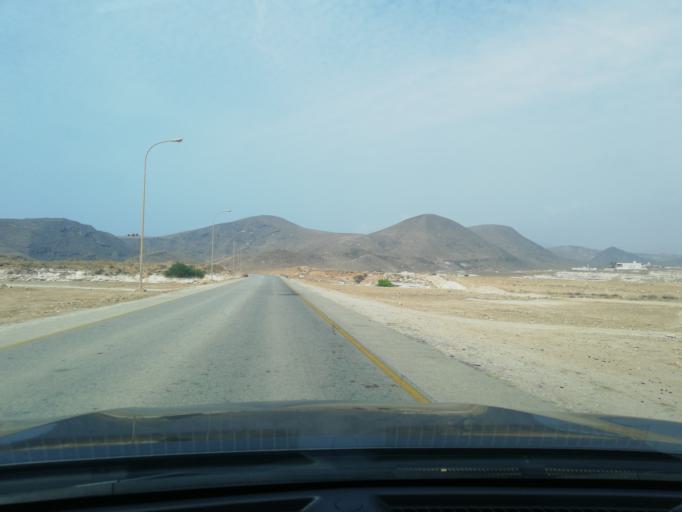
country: OM
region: Zufar
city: Salalah
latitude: 16.9066
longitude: 53.8240
